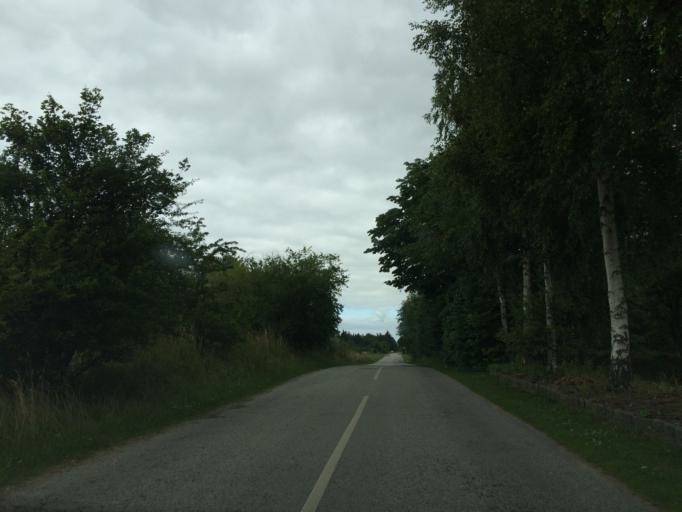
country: DK
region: Central Jutland
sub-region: Silkeborg Kommune
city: Svejbaek
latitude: 56.2140
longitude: 9.6592
